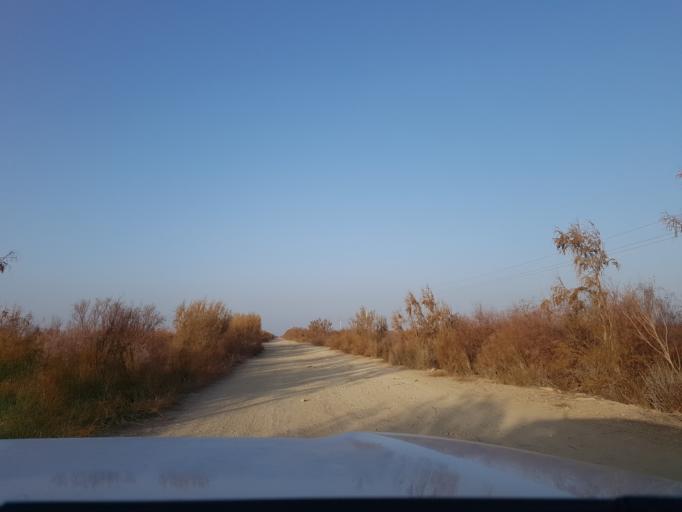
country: TM
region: Dasoguz
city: Koeneuergench
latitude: 41.8525
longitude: 58.2664
